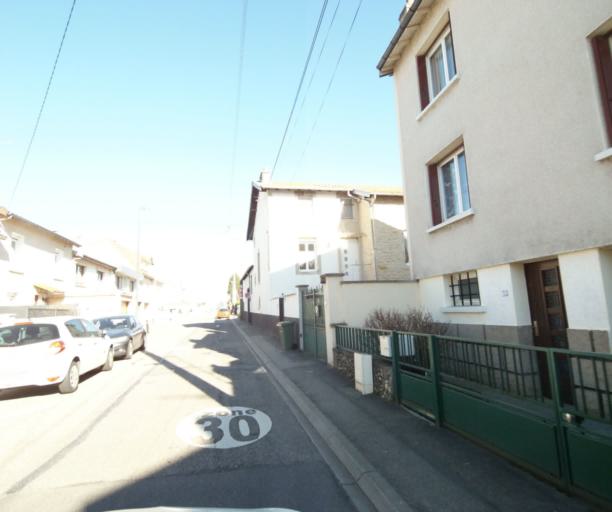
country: FR
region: Lorraine
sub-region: Departement de Meurthe-et-Moselle
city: Tomblaine
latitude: 48.6854
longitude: 6.2161
